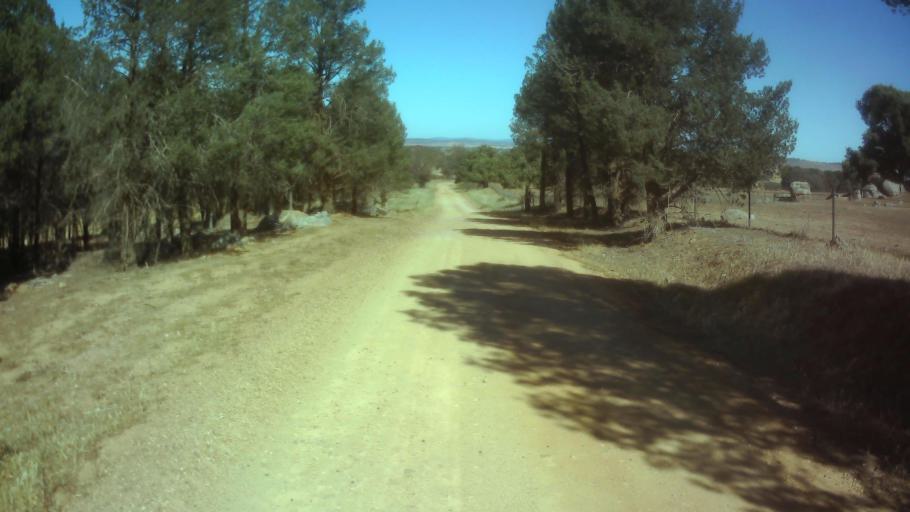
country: AU
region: New South Wales
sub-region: Weddin
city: Grenfell
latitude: -33.9926
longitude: 148.3454
